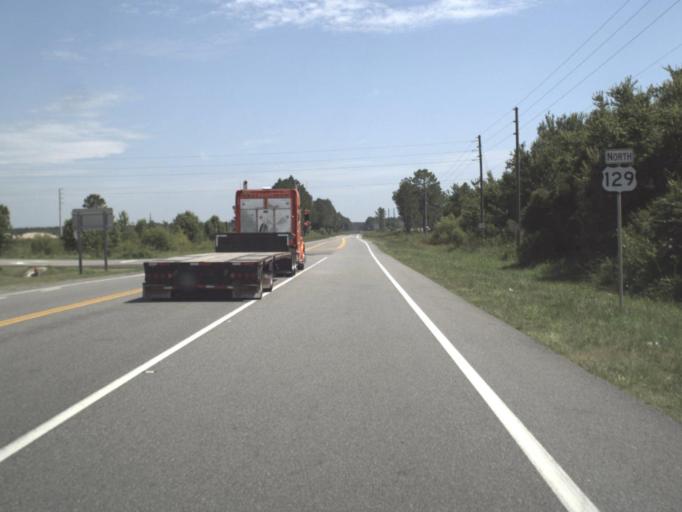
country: US
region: Florida
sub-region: Hamilton County
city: Jasper
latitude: 30.4519
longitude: -82.9326
